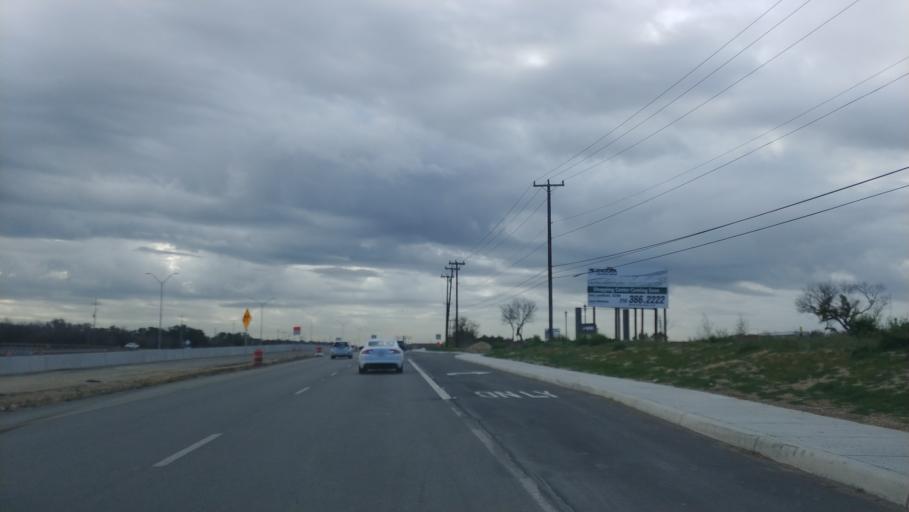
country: US
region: Texas
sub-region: Bexar County
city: Lackland Air Force Base
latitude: 29.4317
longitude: -98.7119
